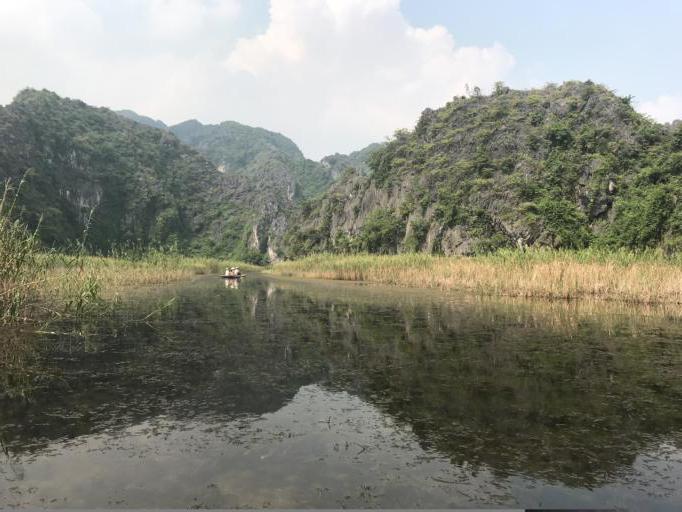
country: VN
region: Ninh Binh
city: Thi Tran Me
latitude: 20.3641
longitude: 105.8898
